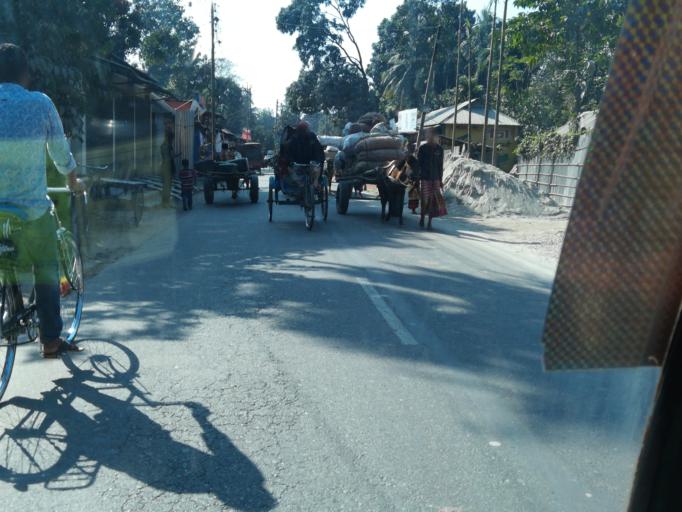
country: BD
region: Rangpur Division
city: Nageswari
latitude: 25.8151
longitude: 89.6509
